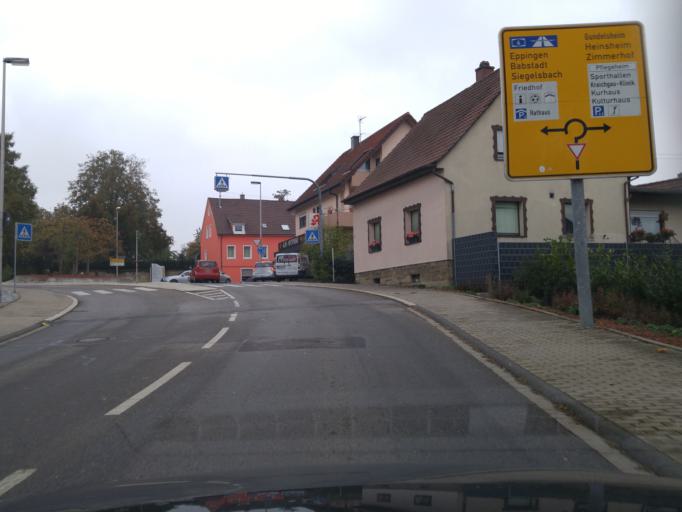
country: DE
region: Baden-Wuerttemberg
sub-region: Regierungsbezirk Stuttgart
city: Bad Rappenau
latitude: 49.2397
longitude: 9.1031
